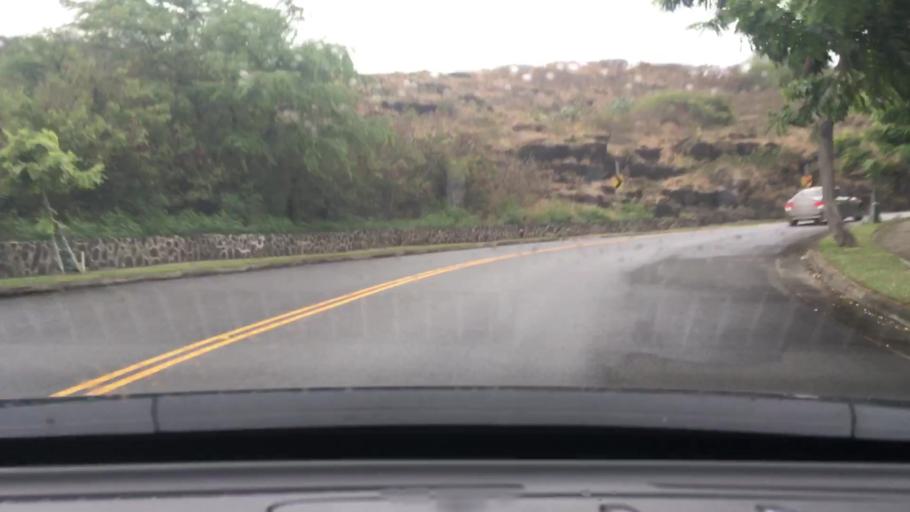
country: US
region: Hawaii
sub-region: Honolulu County
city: Waimanalo Beach
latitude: 21.2896
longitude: -157.7045
